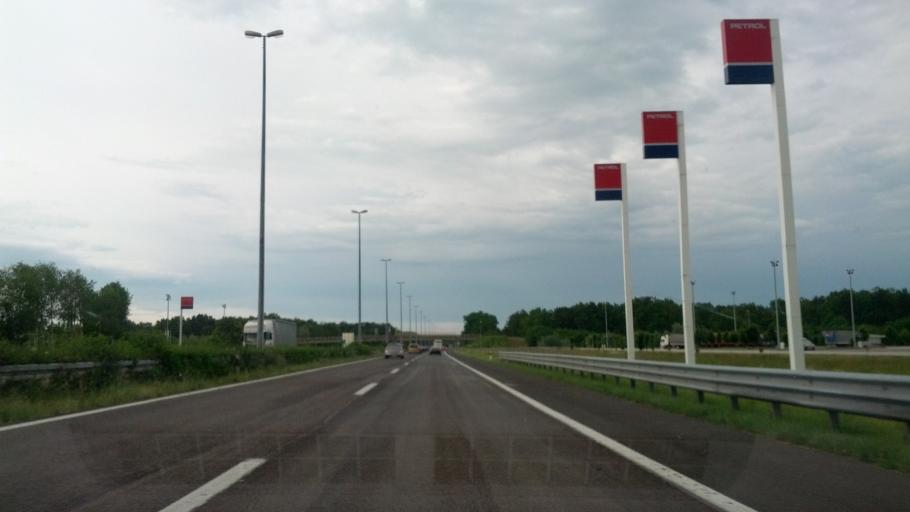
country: HR
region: Zagrebacka
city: Jastrebarsko
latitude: 45.6613
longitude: 15.7084
